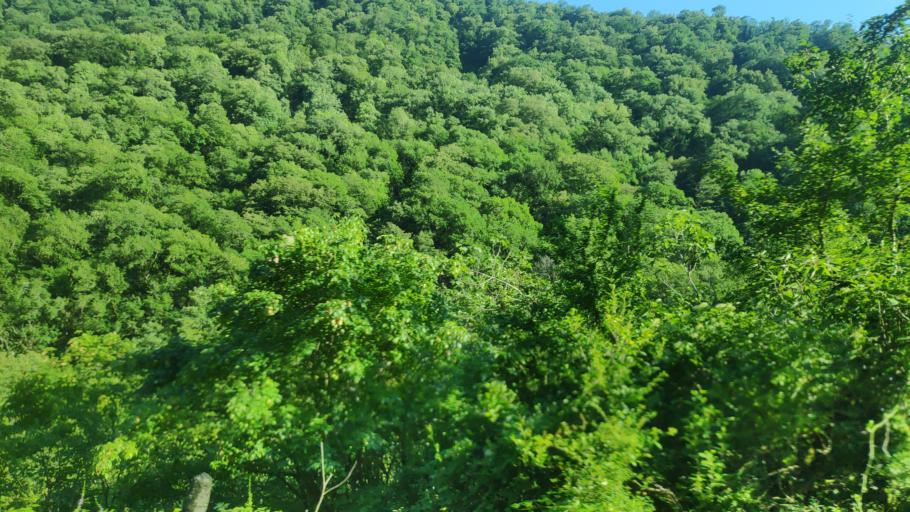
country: GE
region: Abkhazia
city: Gagra
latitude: 43.3530
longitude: 40.4186
